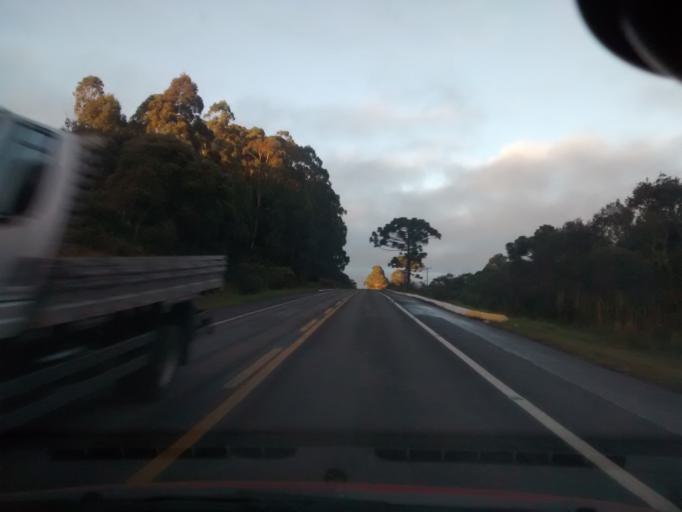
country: BR
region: Rio Grande do Sul
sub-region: Vacaria
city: Estrela
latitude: -28.2561
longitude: -50.7826
